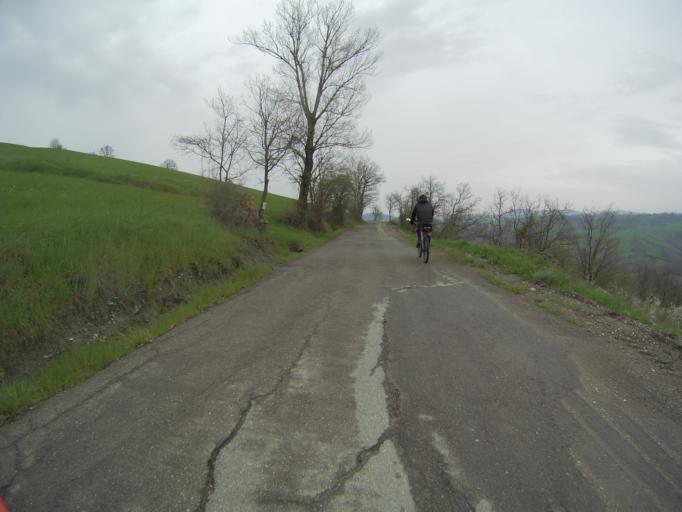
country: IT
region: Emilia-Romagna
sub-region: Provincia di Reggio Emilia
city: Casina
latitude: 44.5363
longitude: 10.4564
